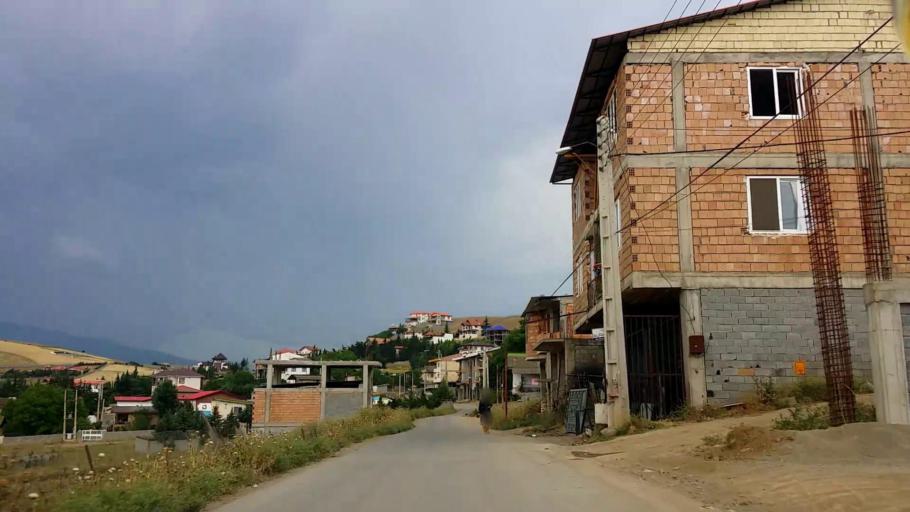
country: IR
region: Mazandaran
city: Chalus
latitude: 36.5143
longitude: 51.2545
